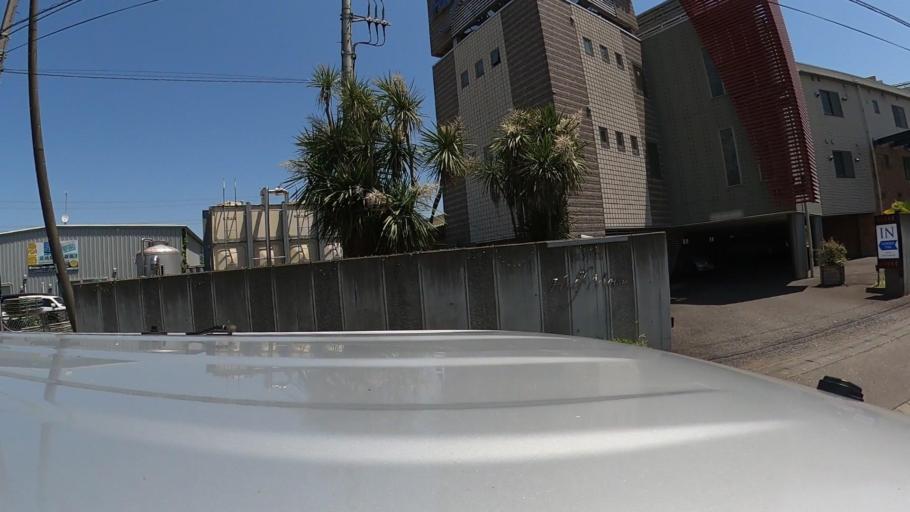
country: JP
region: Ibaraki
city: Ushiku
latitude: 36.0143
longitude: 140.0831
